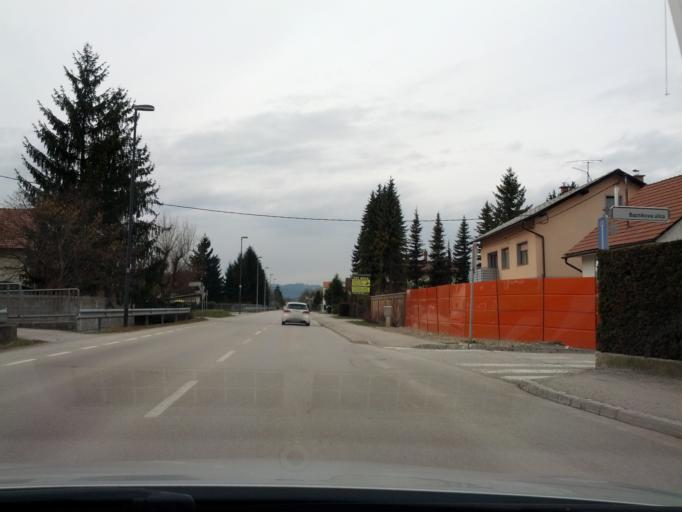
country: SI
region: Ljubljana
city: Ljubljana
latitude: 46.0296
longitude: 14.5211
